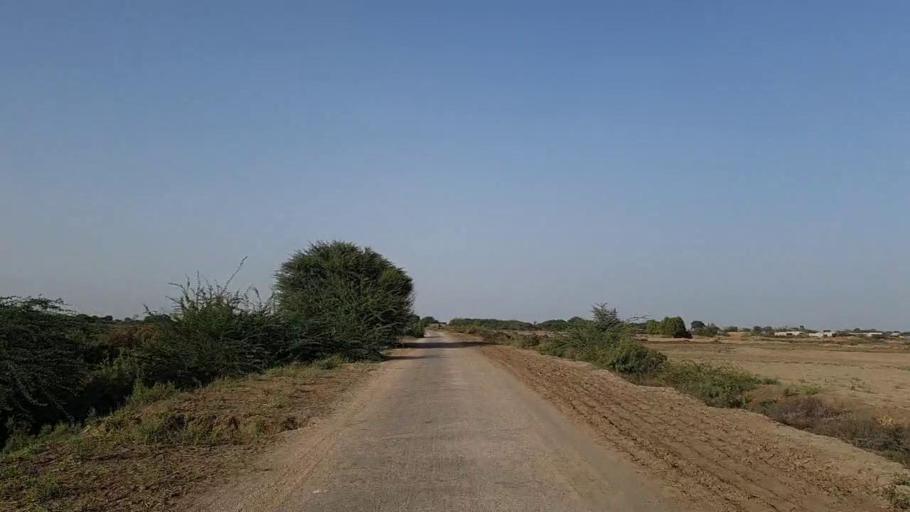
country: PK
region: Sindh
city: Jati
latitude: 24.3101
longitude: 68.1678
